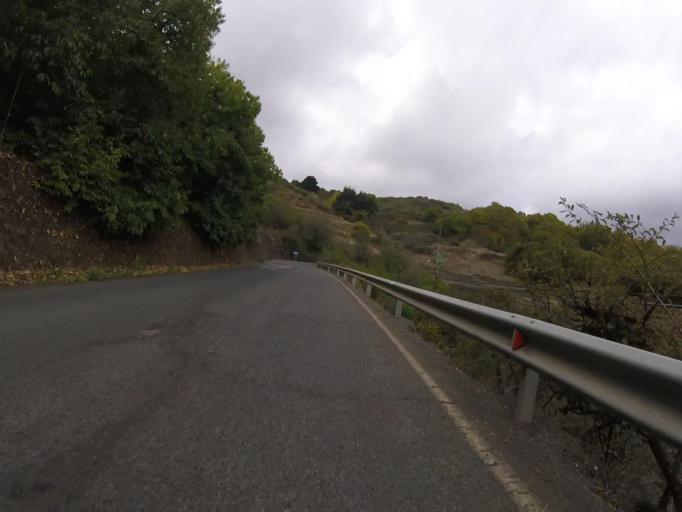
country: ES
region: Canary Islands
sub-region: Provincia de Las Palmas
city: Vega de San Mateo
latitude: 27.9995
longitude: -15.5674
